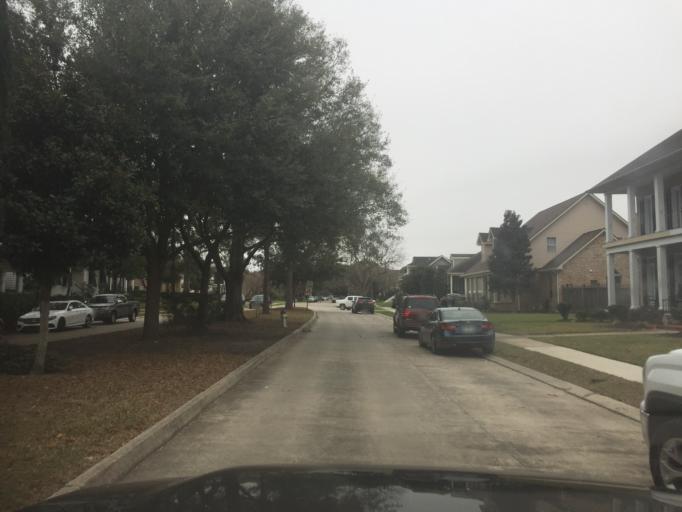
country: US
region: Louisiana
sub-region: Jefferson Parish
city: Metairie
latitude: 29.9999
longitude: -90.1033
